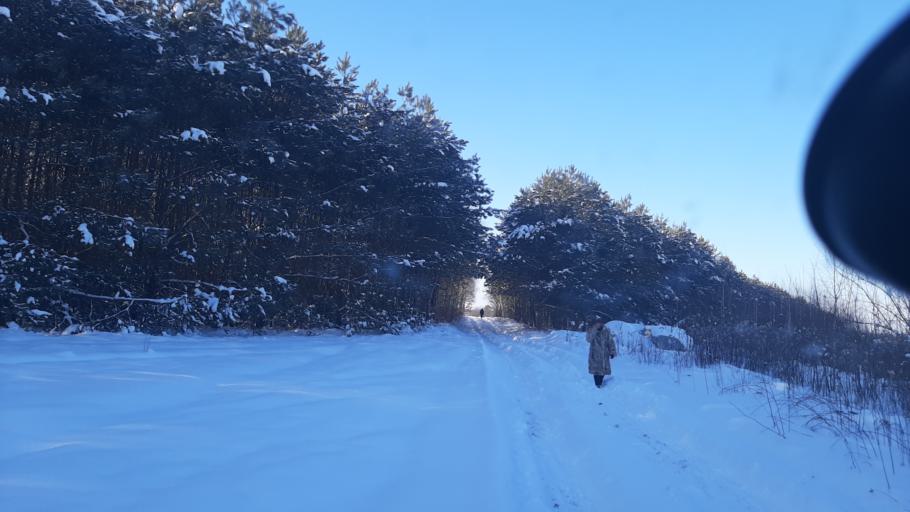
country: PL
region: Lublin Voivodeship
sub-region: Powiat lubelski
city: Jastkow
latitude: 51.3762
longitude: 22.4390
